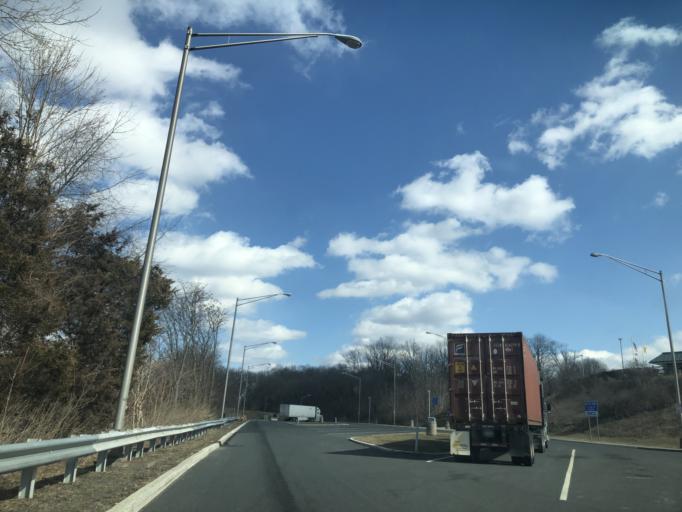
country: US
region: New Jersey
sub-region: Warren County
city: Belvidere
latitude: 40.9272
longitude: -75.0411
